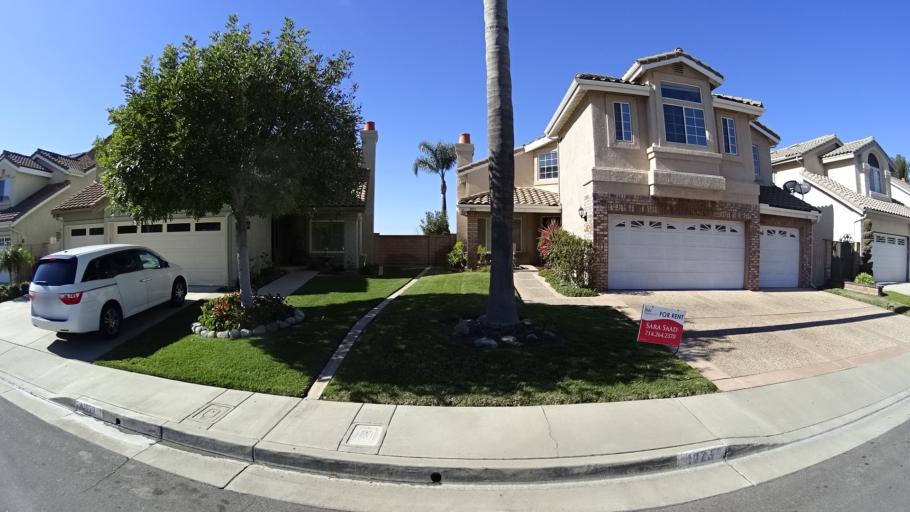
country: US
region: California
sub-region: Orange County
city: Villa Park
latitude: 33.8471
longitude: -117.7434
